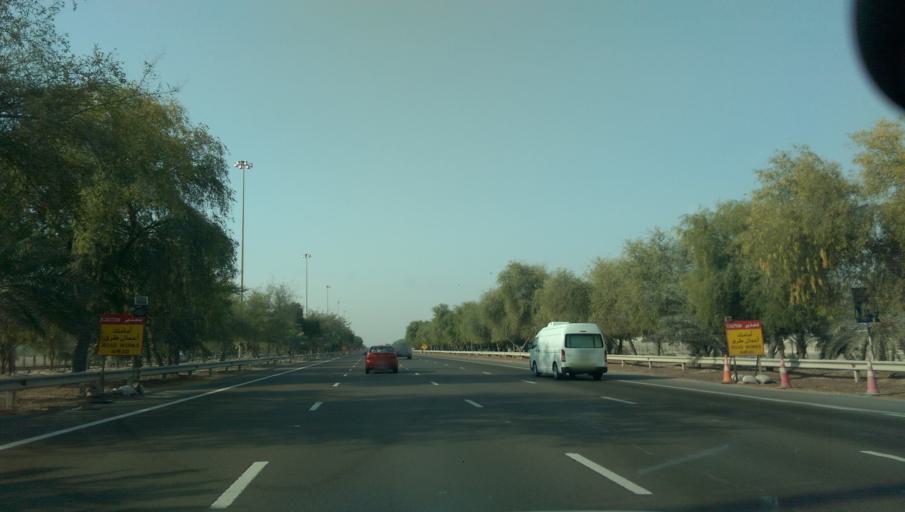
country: AE
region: Abu Dhabi
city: Abu Dhabi
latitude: 24.4482
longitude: 54.6785
